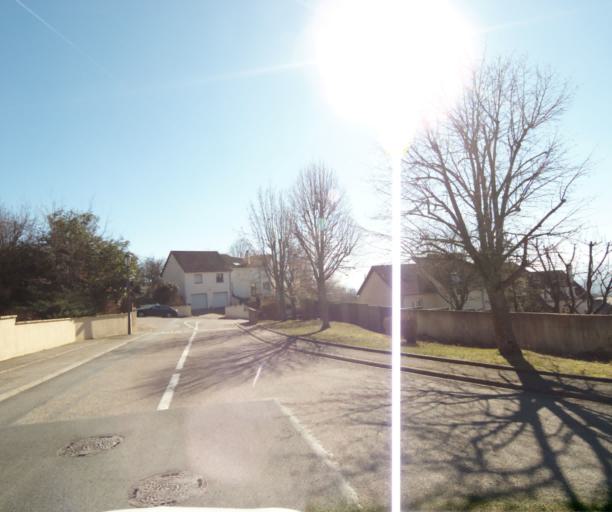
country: FR
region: Lorraine
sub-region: Departement de Meurthe-et-Moselle
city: Essey-les-Nancy
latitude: 48.7120
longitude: 6.2230
